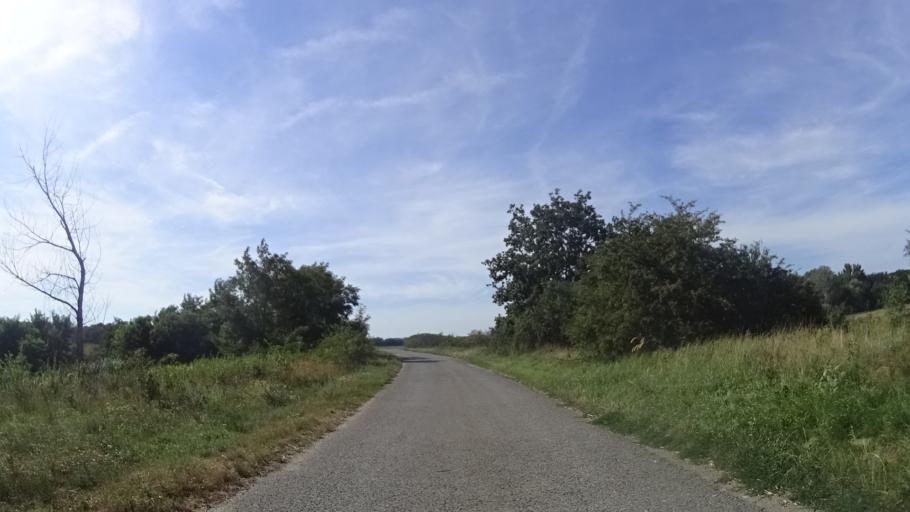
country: AT
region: Lower Austria
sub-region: Politischer Bezirk Ganserndorf
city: Durnkrut
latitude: 48.4227
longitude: 16.8696
